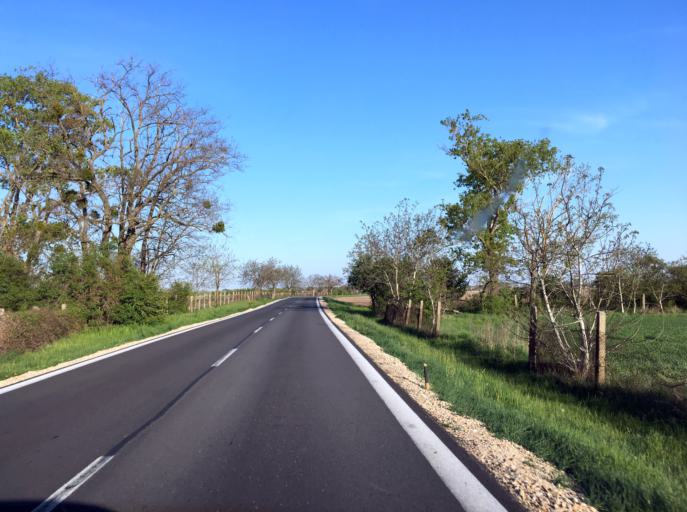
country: AT
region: Burgenland
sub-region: Politischer Bezirk Neusiedl am See
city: Deutsch Jahrndorf
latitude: 48.0622
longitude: 17.1247
